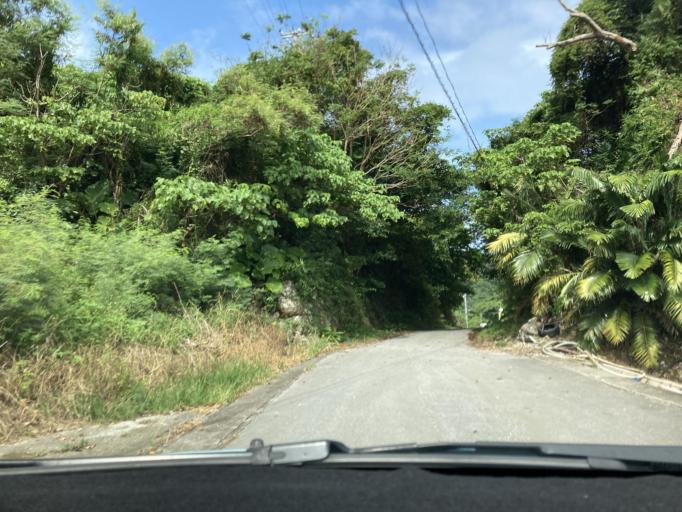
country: JP
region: Okinawa
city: Ginowan
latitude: 26.1583
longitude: 127.8082
